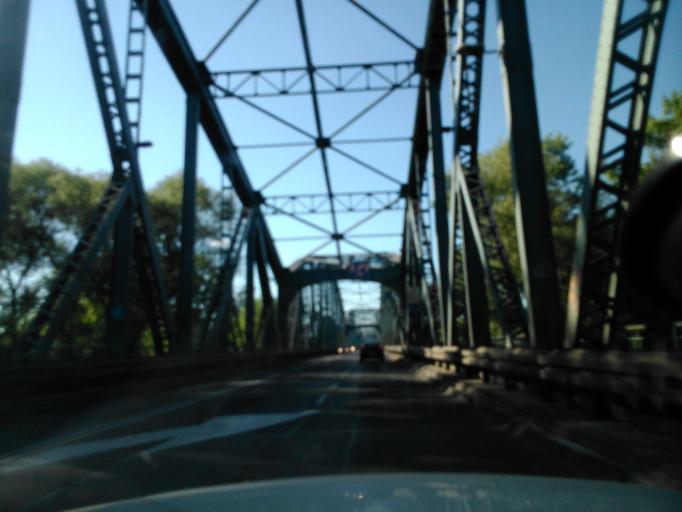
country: PL
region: Kujawsko-Pomorskie
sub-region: Torun
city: Torun
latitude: 53.0019
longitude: 18.6035
